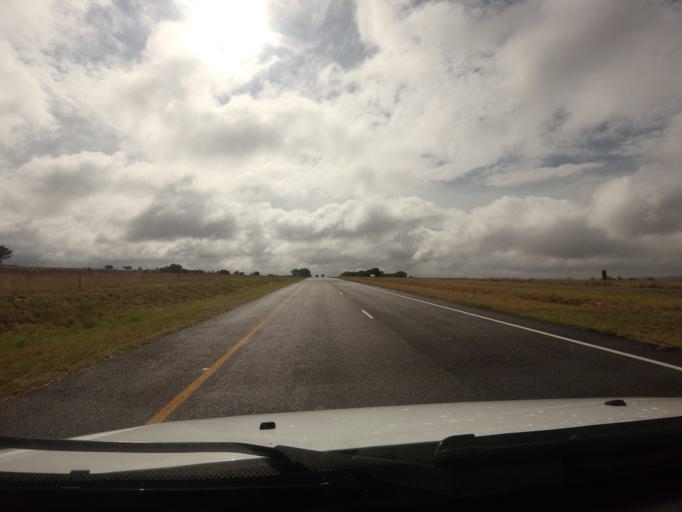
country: ZA
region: Gauteng
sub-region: City of Tshwane Metropolitan Municipality
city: Bronkhorstspruit
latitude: -25.7991
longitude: 28.6251
